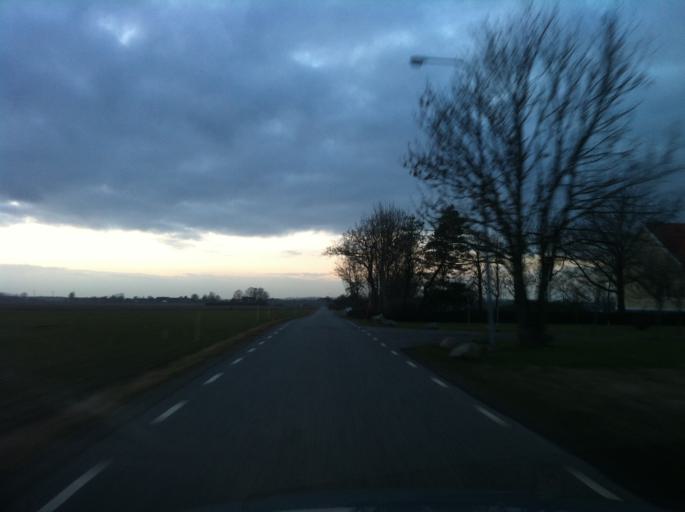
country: SE
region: Skane
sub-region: Svalovs Kommun
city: Teckomatorp
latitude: 55.8663
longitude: 13.0294
